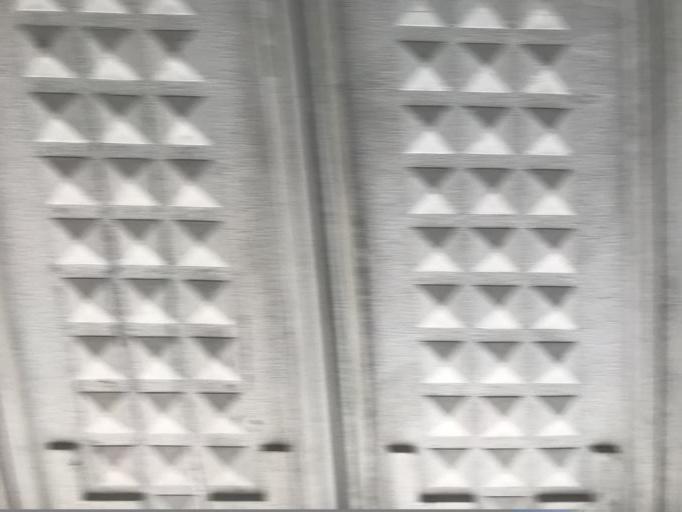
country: TR
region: Istanbul
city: Bahcelievler
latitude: 40.9673
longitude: 28.7976
